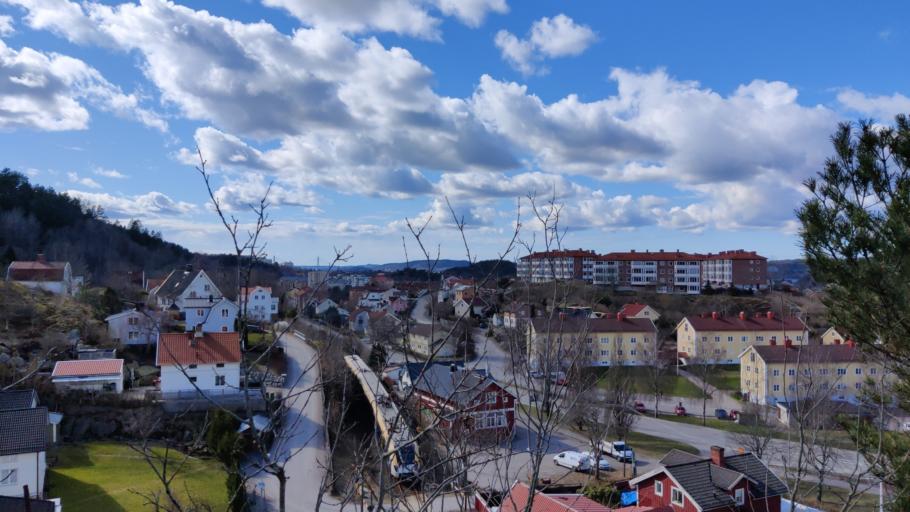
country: SE
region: Vaestra Goetaland
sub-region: Uddevalla Kommun
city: Uddevalla
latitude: 58.3454
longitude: 11.9425
